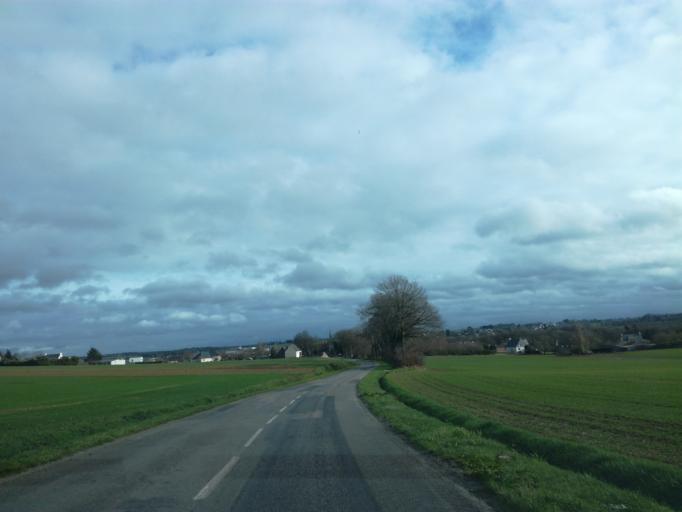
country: FR
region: Brittany
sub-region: Departement du Morbihan
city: Le Sourn
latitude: 48.0406
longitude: -2.9768
